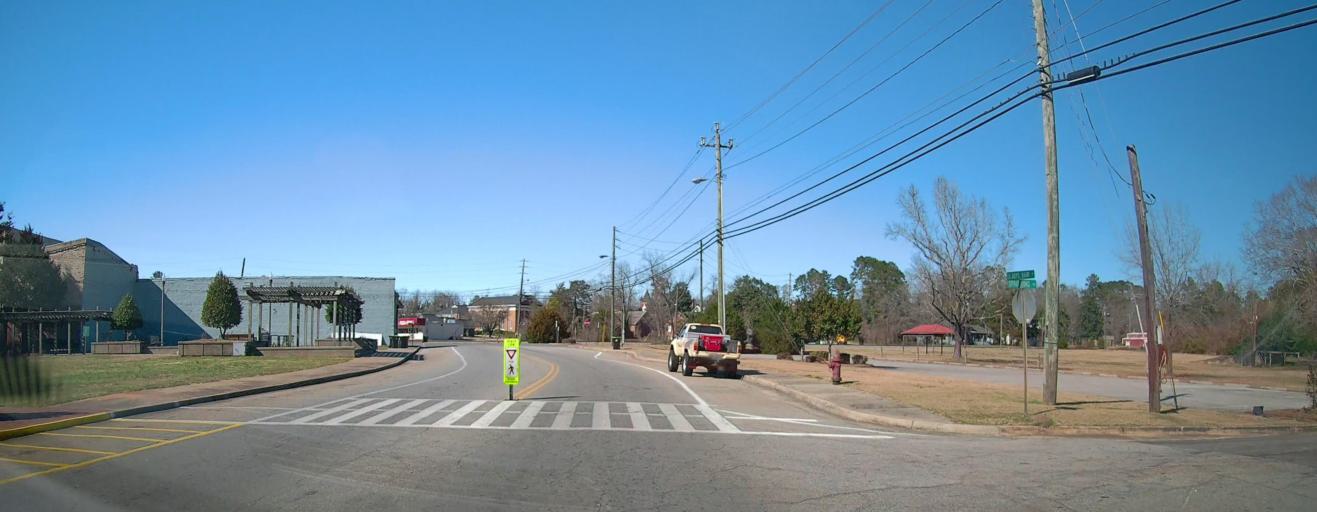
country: US
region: Georgia
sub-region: Macon County
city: Montezuma
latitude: 32.2999
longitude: -84.0286
